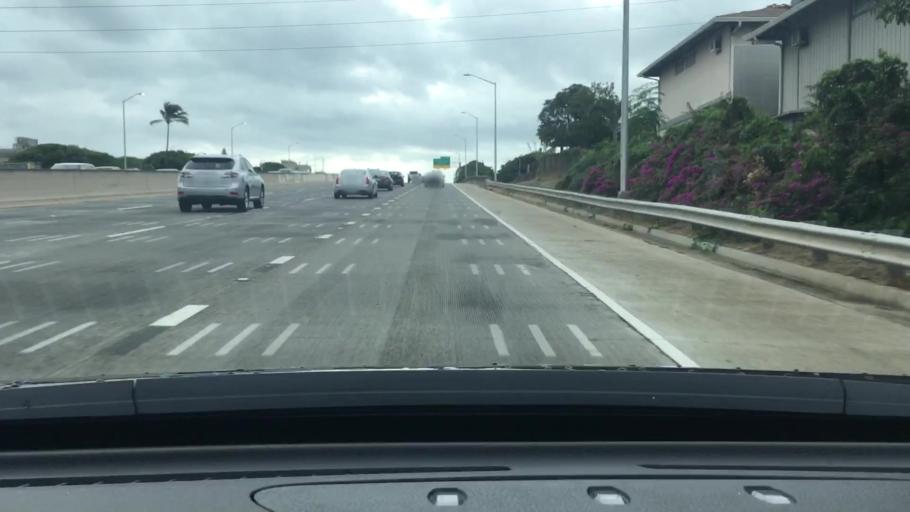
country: US
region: Hawaii
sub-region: Honolulu County
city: Honolulu
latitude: 21.2823
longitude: -157.8044
